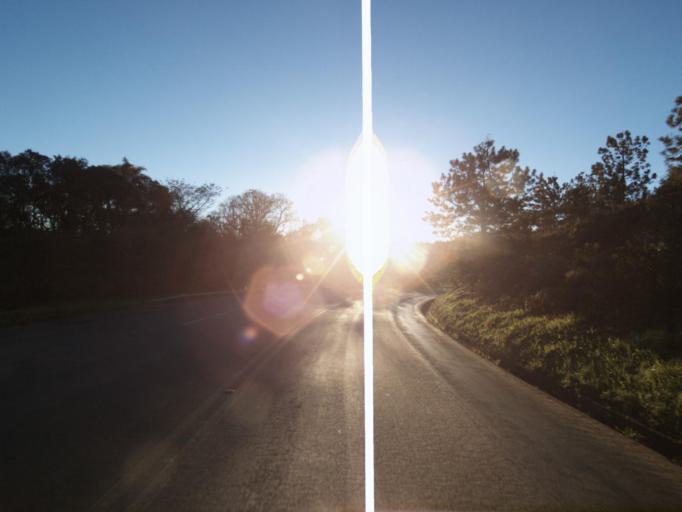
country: BR
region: Santa Catarina
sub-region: Sao Lourenco Do Oeste
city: Sao Lourenco dOeste
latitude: -26.8262
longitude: -53.1014
